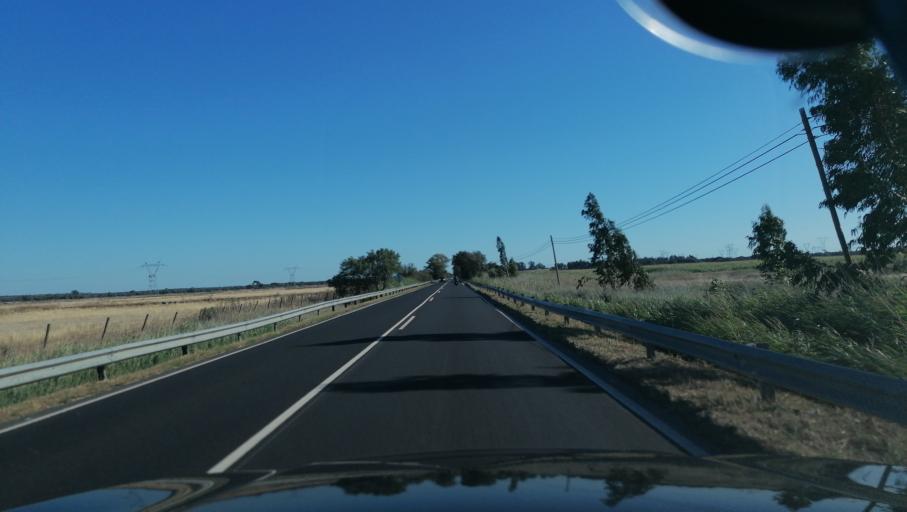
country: PT
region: Santarem
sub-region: Benavente
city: Samora Correia
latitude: 38.8802
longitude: -8.8813
